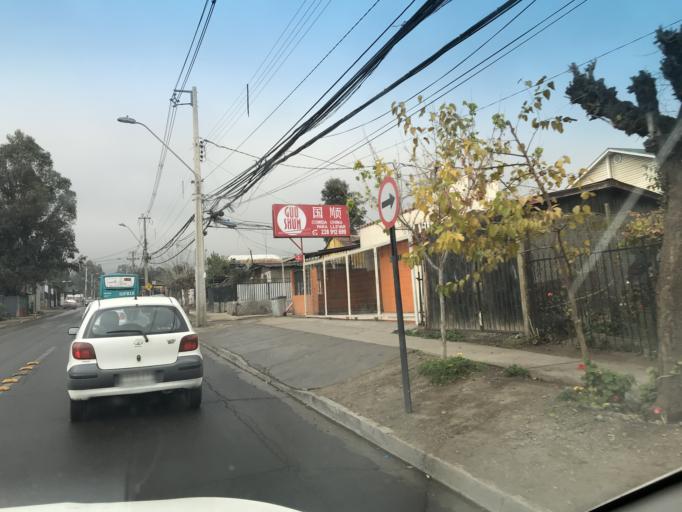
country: CL
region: Santiago Metropolitan
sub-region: Provincia de Santiago
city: Villa Presidente Frei, Nunoa, Santiago, Chile
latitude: -33.5121
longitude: -70.5547
